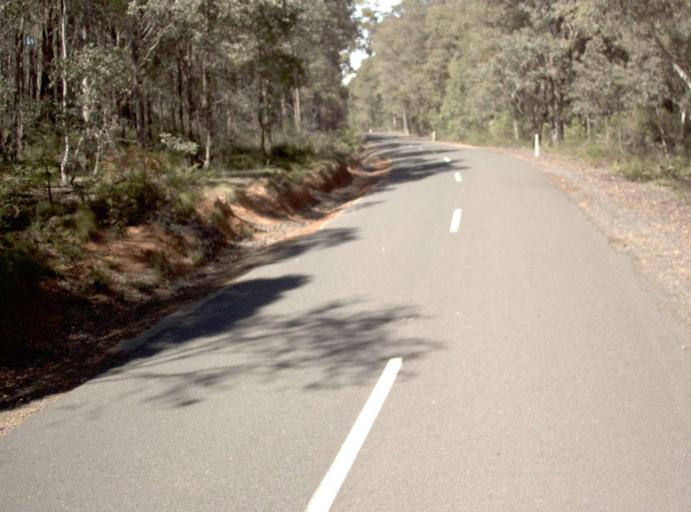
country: AU
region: New South Wales
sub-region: Bombala
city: Bombala
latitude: -37.0943
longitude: 148.7644
